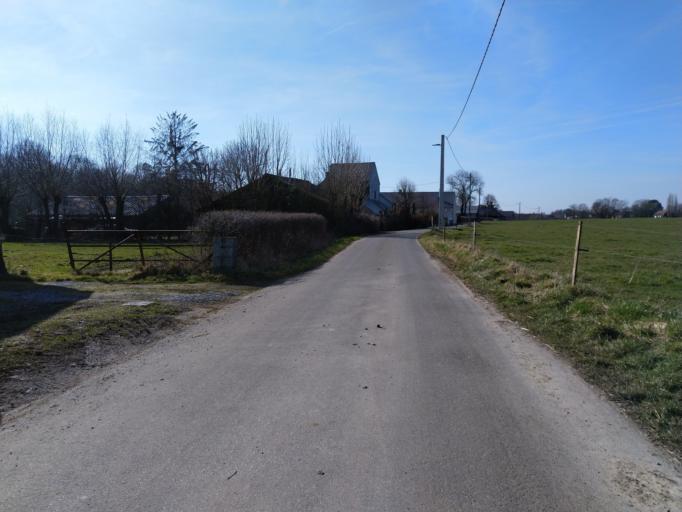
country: FR
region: Nord-Pas-de-Calais
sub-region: Departement du Nord
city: Feignies
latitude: 50.3289
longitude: 3.8903
